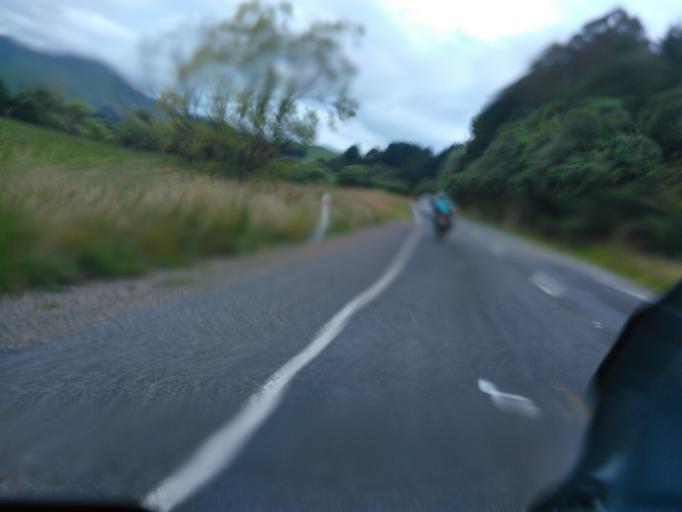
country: NZ
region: Bay of Plenty
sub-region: Opotiki District
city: Opotiki
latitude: -38.3641
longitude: 177.5093
